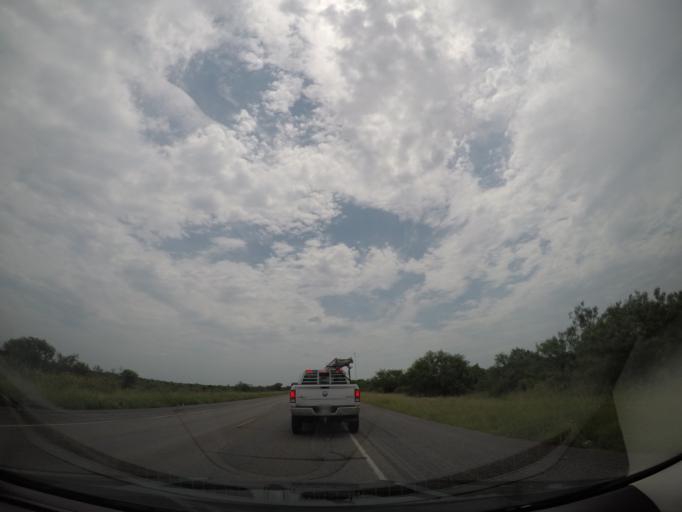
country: US
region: Texas
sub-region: Val Verde County
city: Laughlin Air Force Base
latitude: 29.3865
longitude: -100.7457
